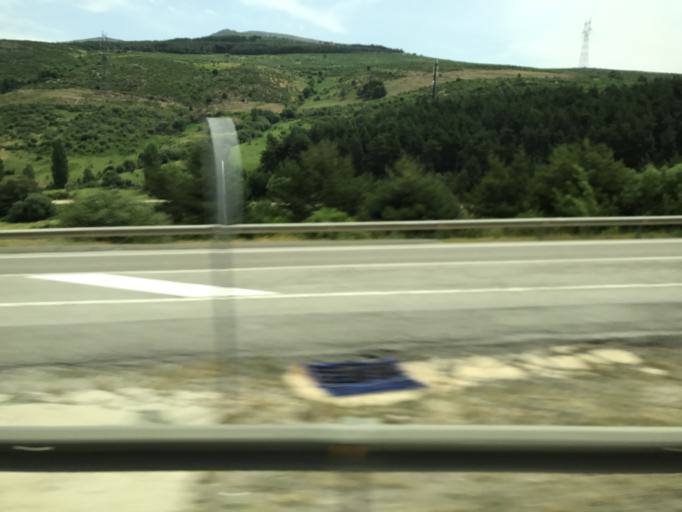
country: ES
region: Madrid
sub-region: Provincia de Madrid
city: Somosierra
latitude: 41.1381
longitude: -3.5820
